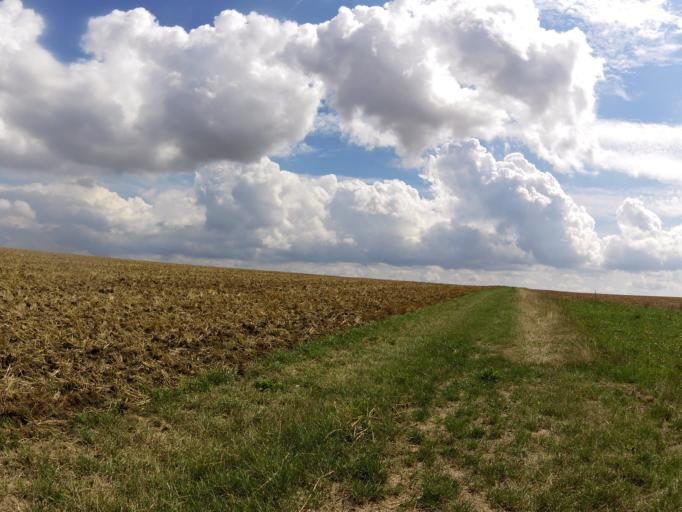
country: DE
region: Bavaria
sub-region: Regierungsbezirk Unterfranken
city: Geroldshausen
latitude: 49.6953
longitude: 9.8942
